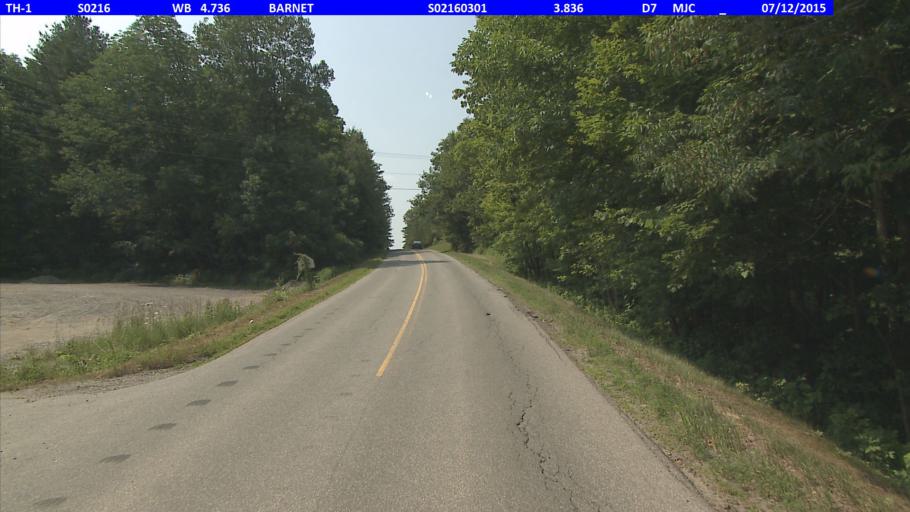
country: US
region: Vermont
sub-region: Caledonia County
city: Saint Johnsbury
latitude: 44.3052
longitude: -72.0824
